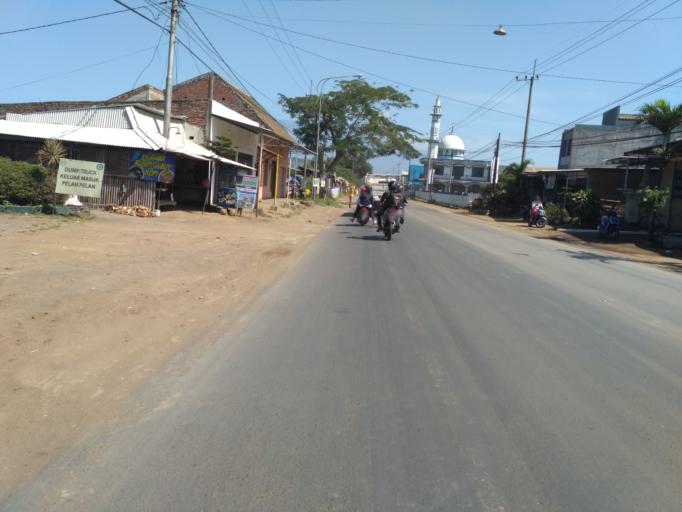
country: ID
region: East Java
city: Tamiajeng
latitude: -7.9533
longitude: 112.6956
